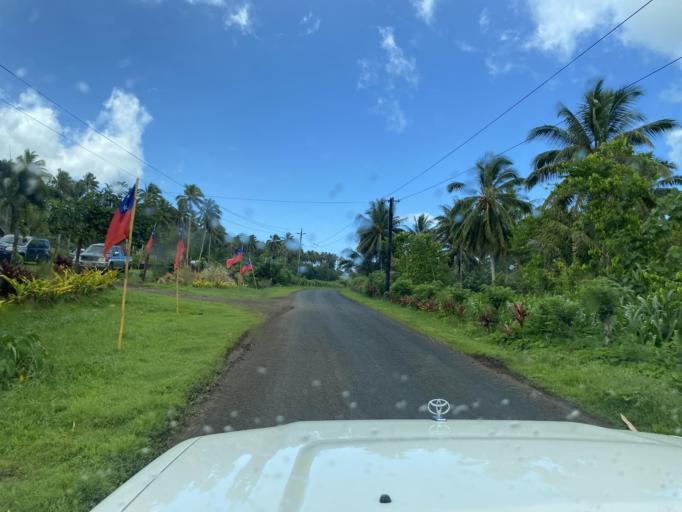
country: WS
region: Va`a-o-Fonoti
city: Samamea
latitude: -13.9804
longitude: -171.5880
